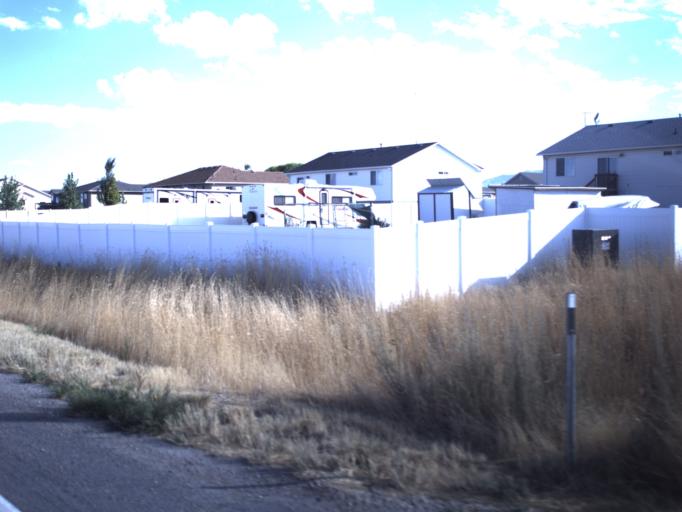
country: US
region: Utah
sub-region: Tooele County
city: Grantsville
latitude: 40.6061
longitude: -112.4885
